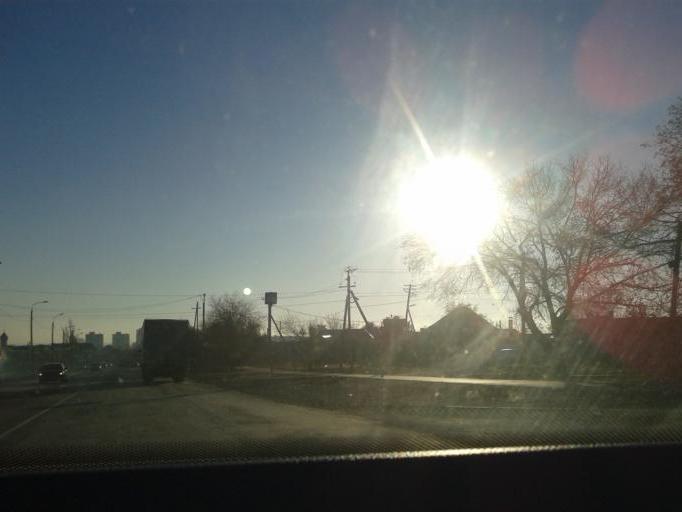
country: RU
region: Volgograd
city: Volgograd
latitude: 48.7024
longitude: 44.4582
